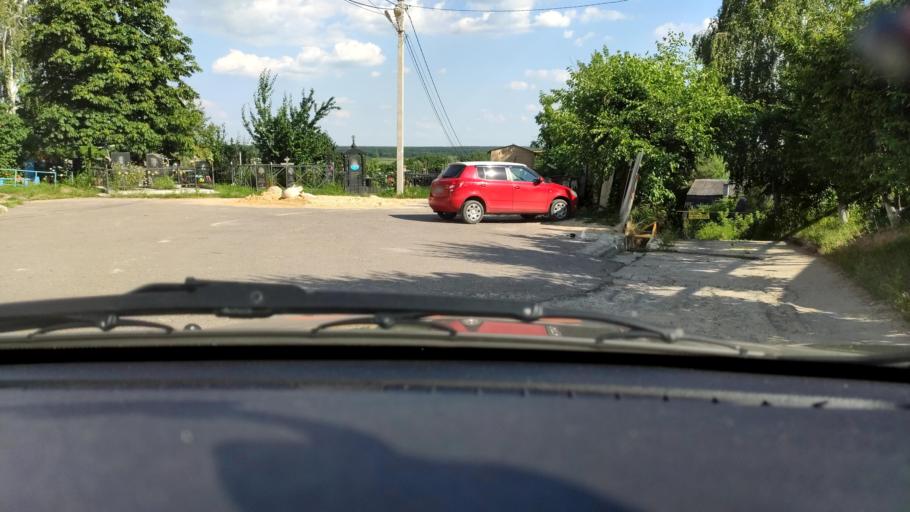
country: RU
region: Voronezj
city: Ramon'
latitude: 51.8207
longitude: 39.2775
